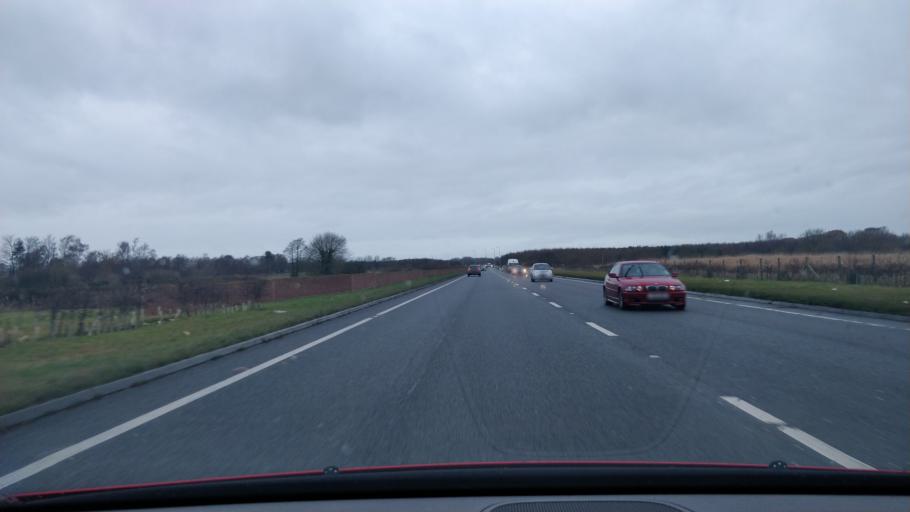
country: GB
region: England
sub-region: Sefton
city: Thornton
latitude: 53.5012
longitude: -2.9881
